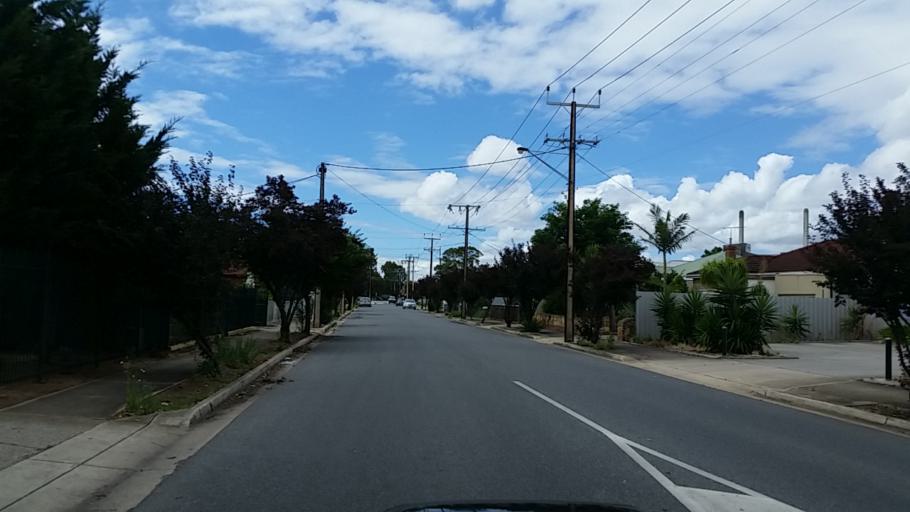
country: AU
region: South Australia
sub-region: Charles Sturt
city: Allenby Gardens
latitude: -34.8925
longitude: 138.5490
